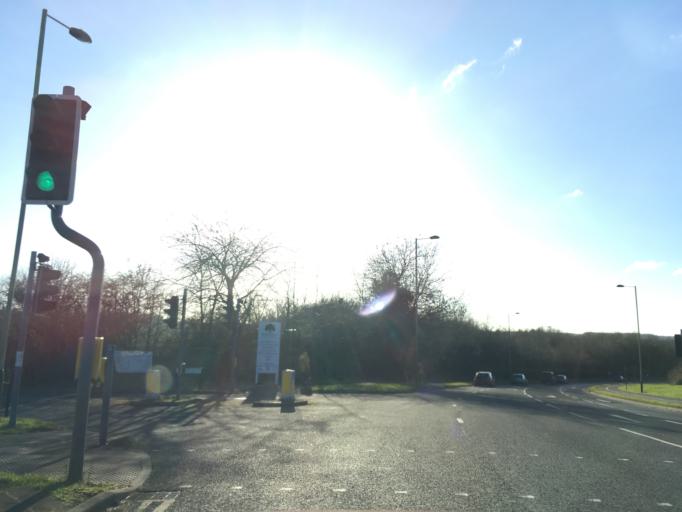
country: GB
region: England
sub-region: Borough of Swindon
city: Swindon
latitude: 51.5401
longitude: -1.7711
